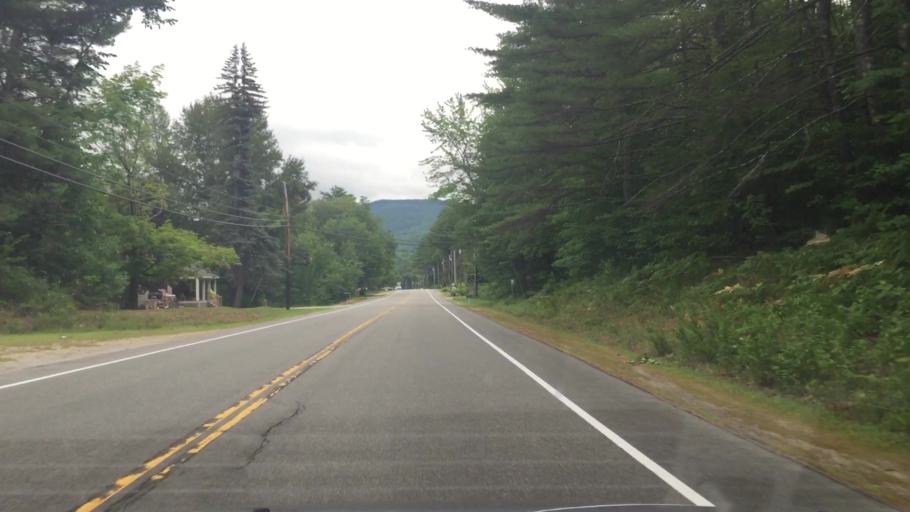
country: US
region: New Hampshire
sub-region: Carroll County
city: Tamworth
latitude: 43.8275
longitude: -71.3217
